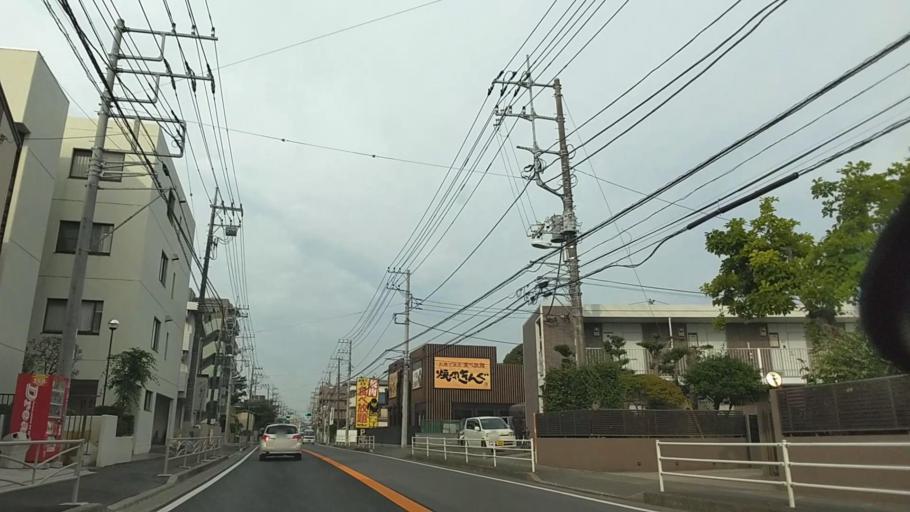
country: JP
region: Kanagawa
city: Fujisawa
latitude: 35.3407
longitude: 139.4369
